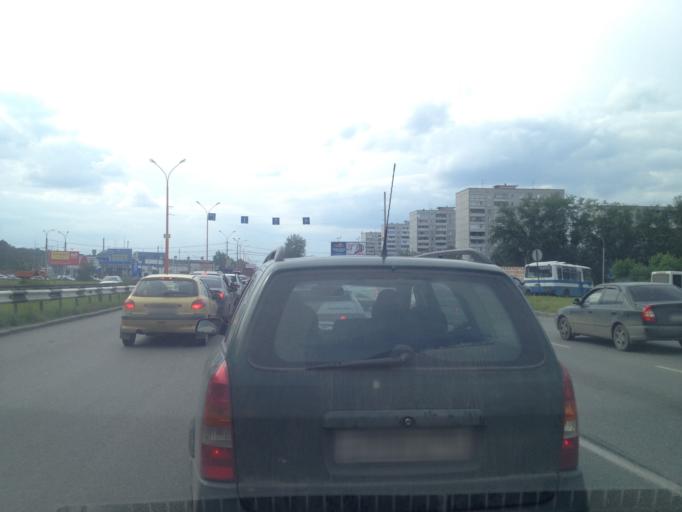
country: RU
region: Sverdlovsk
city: Sovkhoznyy
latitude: 56.7908
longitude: 60.5754
